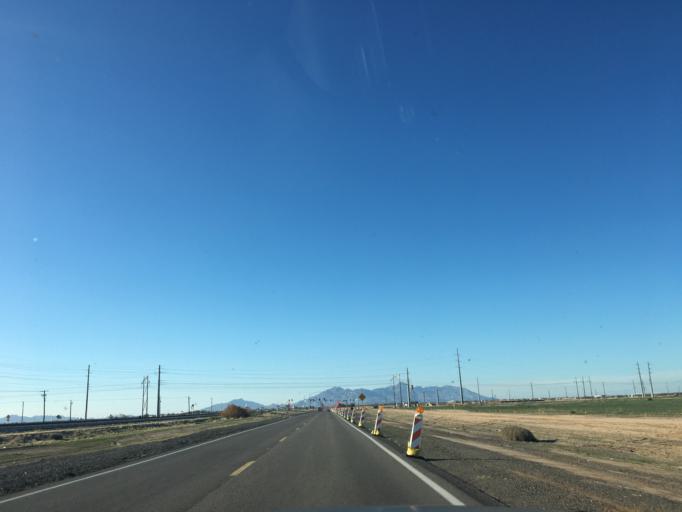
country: US
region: Arizona
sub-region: Pinal County
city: Maricopa
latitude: 33.0228
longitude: -111.9930
